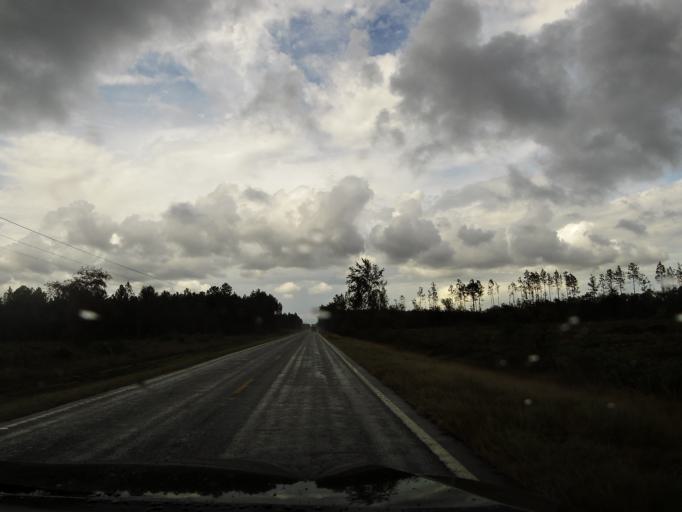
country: US
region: Florida
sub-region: Nassau County
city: Hilliard
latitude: 30.5548
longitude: -82.0419
